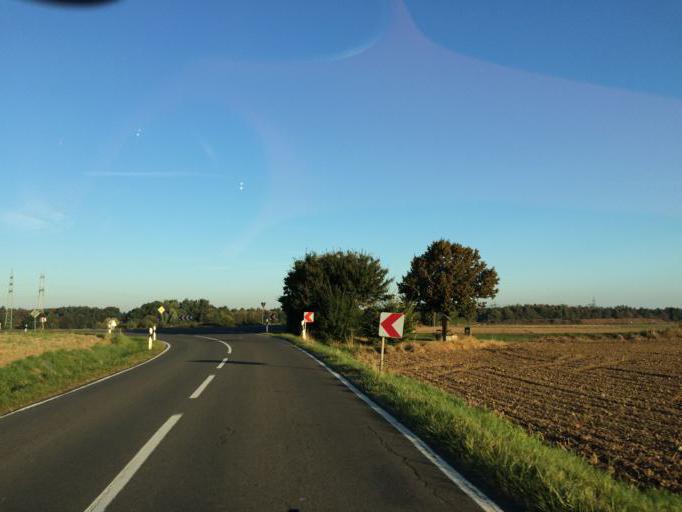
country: DE
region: North Rhine-Westphalia
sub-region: Regierungsbezirk Koln
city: Wachtberg
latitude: 50.6364
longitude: 7.1390
